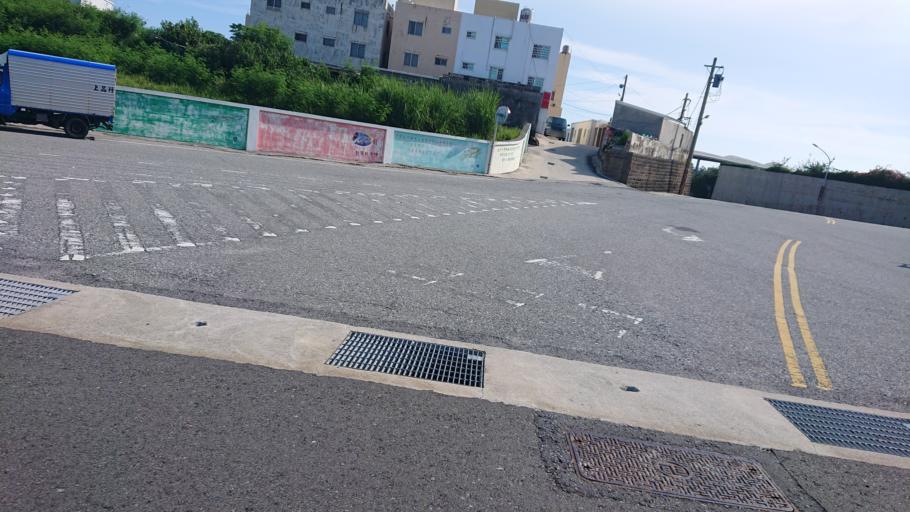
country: TW
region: Taiwan
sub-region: Penghu
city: Ma-kung
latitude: 23.5270
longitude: 119.5690
